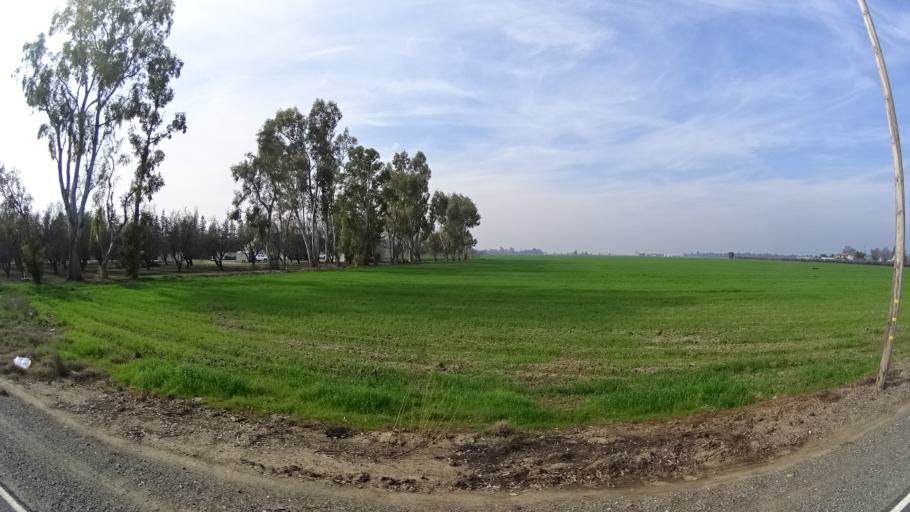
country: US
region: California
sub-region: Yolo County
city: Davis
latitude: 38.5768
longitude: -121.7482
